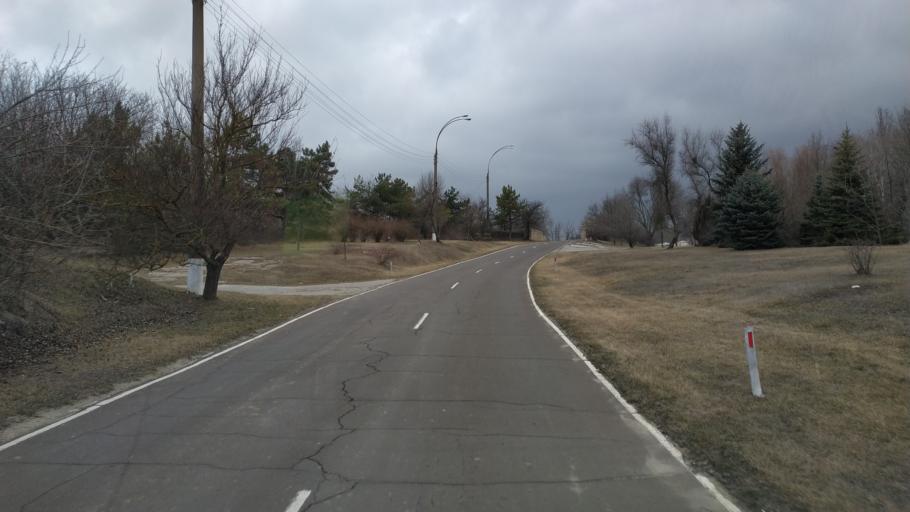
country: MD
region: Laloveni
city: Ialoveni
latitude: 46.9240
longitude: 28.8167
